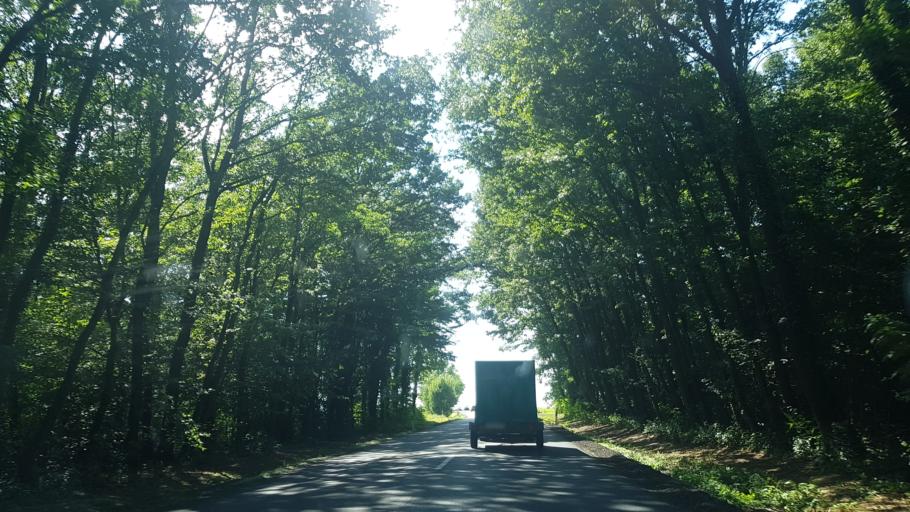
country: HU
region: Somogy
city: Bohonye
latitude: 46.4702
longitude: 17.3883
